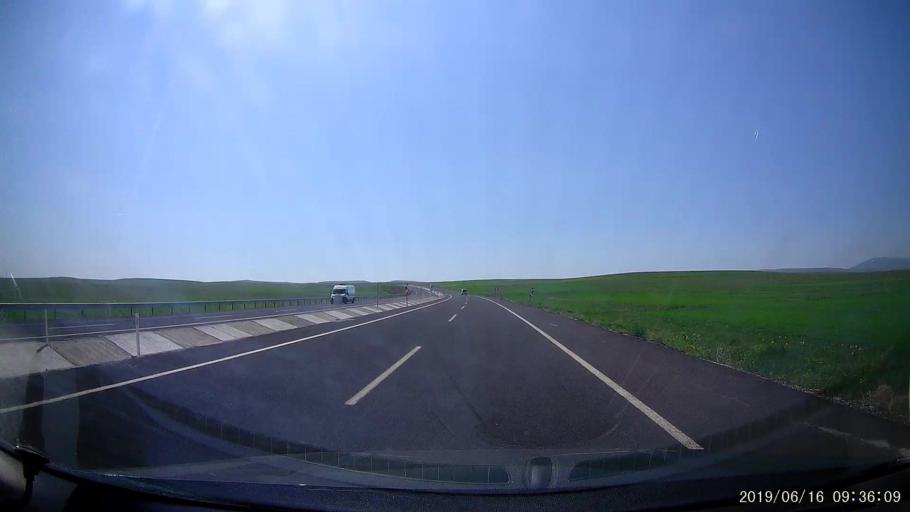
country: TR
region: Kars
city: Kars
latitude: 40.5609
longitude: 43.1674
